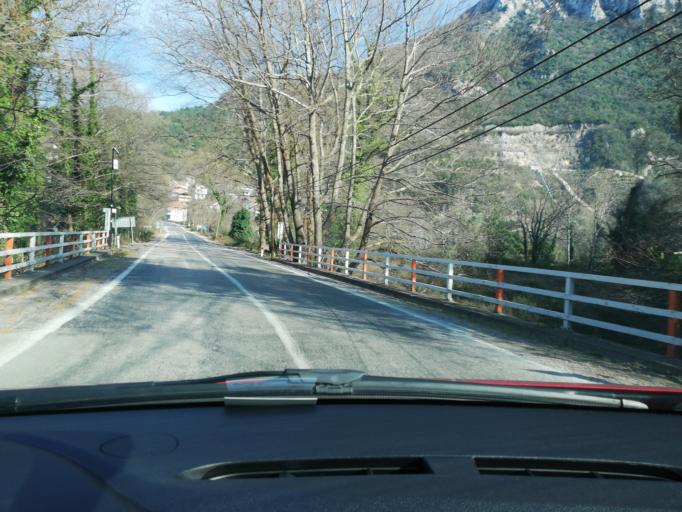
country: TR
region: Bartin
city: Kurucasile
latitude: 41.8439
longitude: 32.7520
